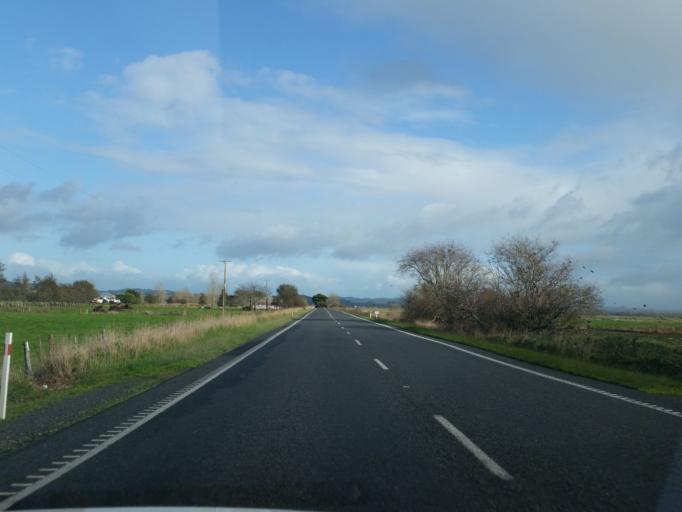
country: NZ
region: Waikato
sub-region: Hauraki District
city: Ngatea
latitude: -37.2761
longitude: 175.4707
